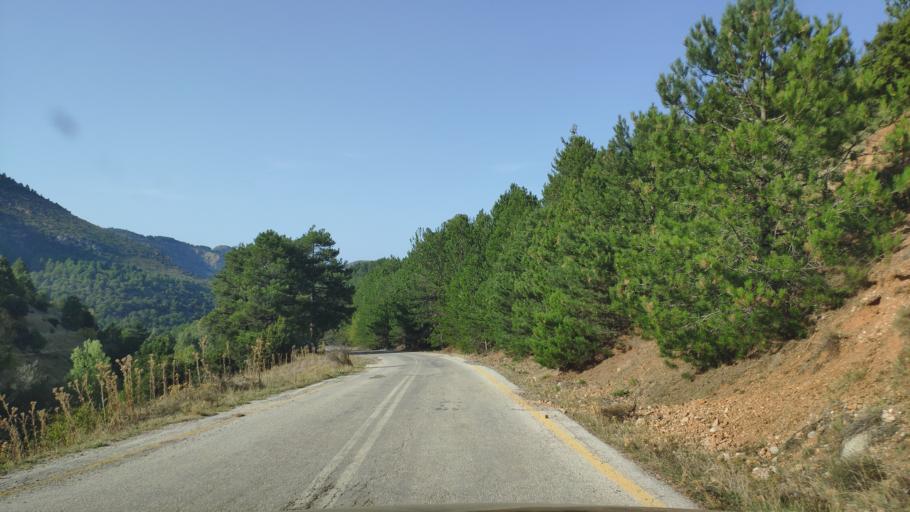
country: GR
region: West Greece
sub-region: Nomos Achaias
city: Aiyira
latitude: 38.0492
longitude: 22.3846
